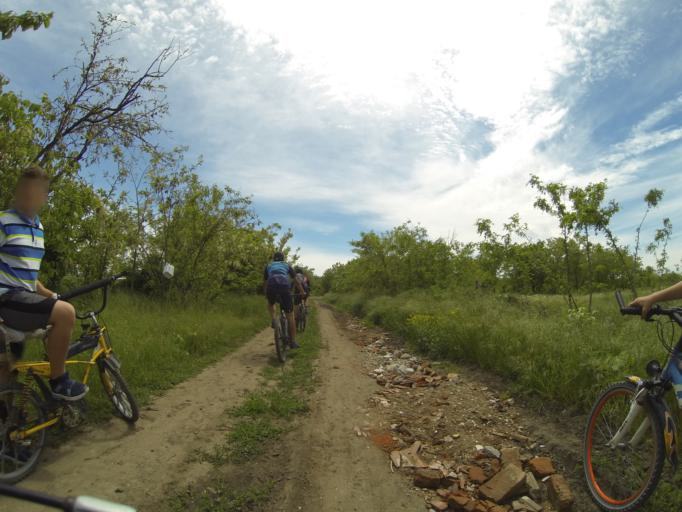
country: RO
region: Dolj
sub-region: Comuna Leu
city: Leu
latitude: 44.1998
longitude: 24.0027
